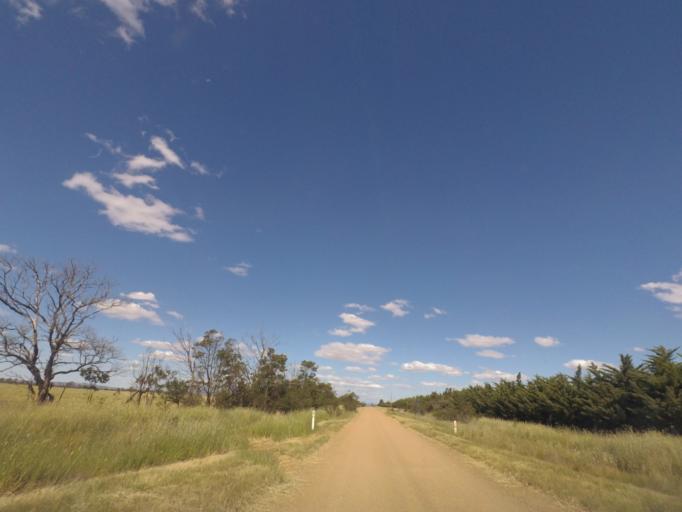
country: AU
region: Victoria
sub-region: Hume
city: Sunbury
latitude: -37.4606
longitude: 144.8062
